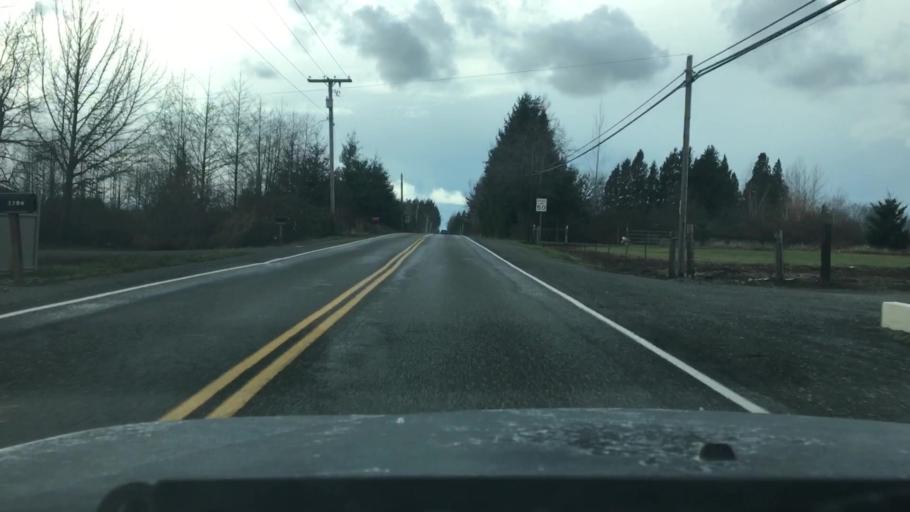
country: US
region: Washington
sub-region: Whatcom County
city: Ferndale
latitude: 48.8483
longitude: -122.6610
